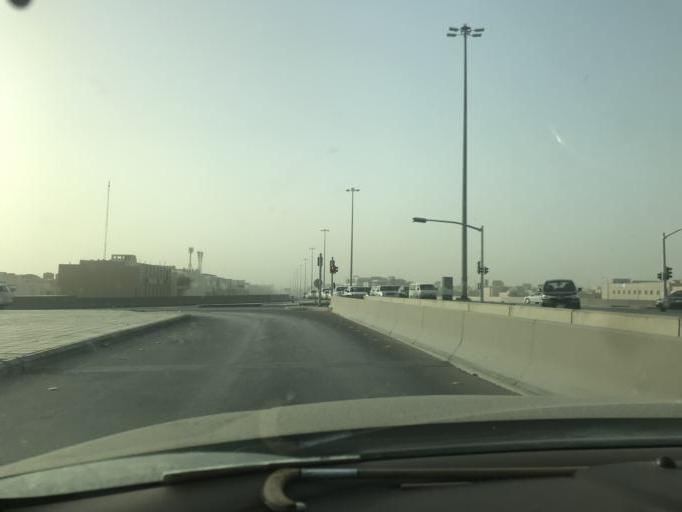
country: SA
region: Ar Riyad
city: Riyadh
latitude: 24.8357
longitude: 46.6352
